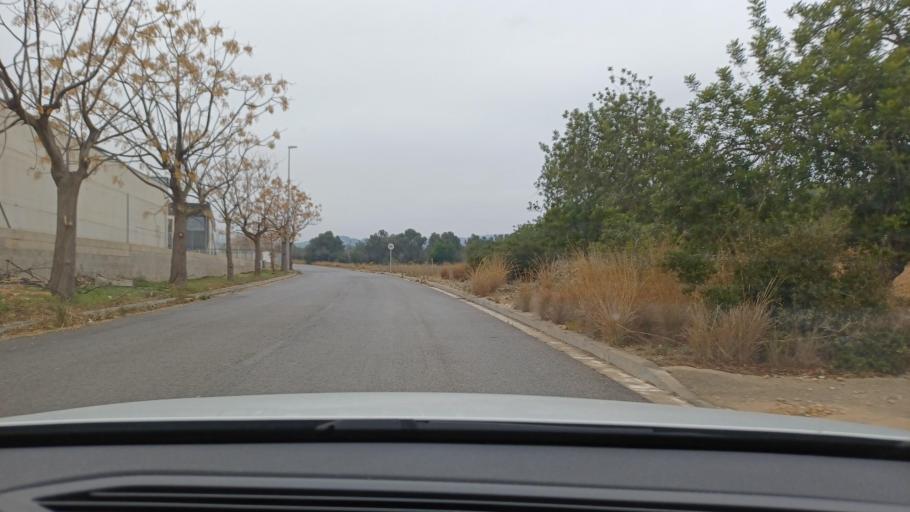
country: ES
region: Catalonia
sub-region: Provincia de Tarragona
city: Amposta
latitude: 40.7676
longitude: 0.5972
